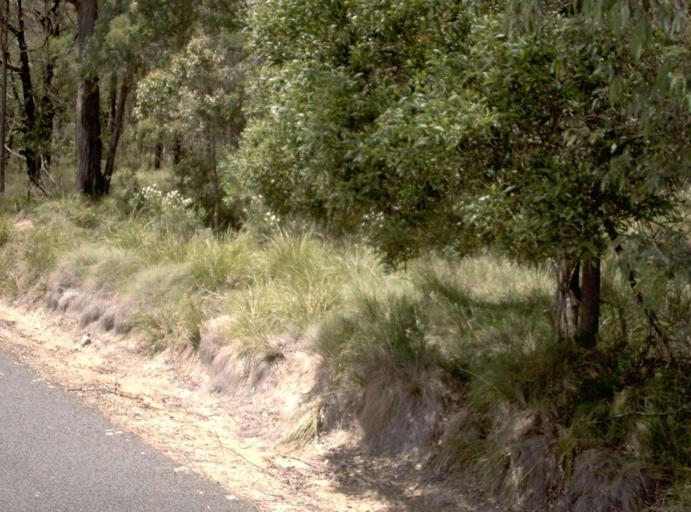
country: AU
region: New South Wales
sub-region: Bombala
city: Bombala
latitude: -37.3966
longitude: 149.0148
